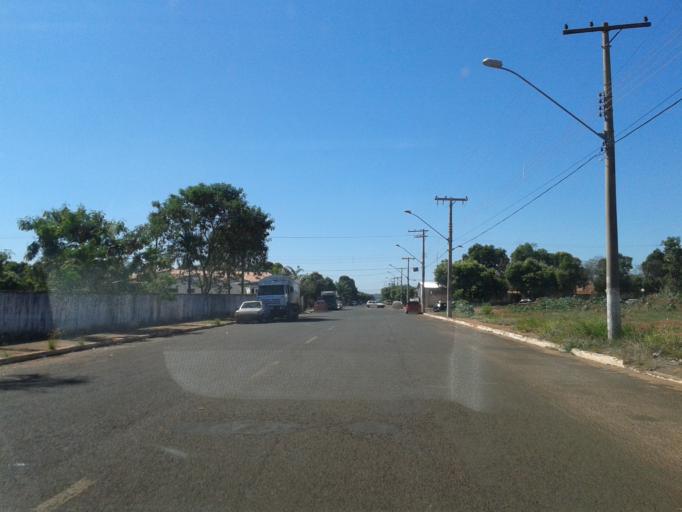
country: BR
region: Minas Gerais
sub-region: Santa Vitoria
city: Santa Vitoria
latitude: -18.8485
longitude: -50.1293
